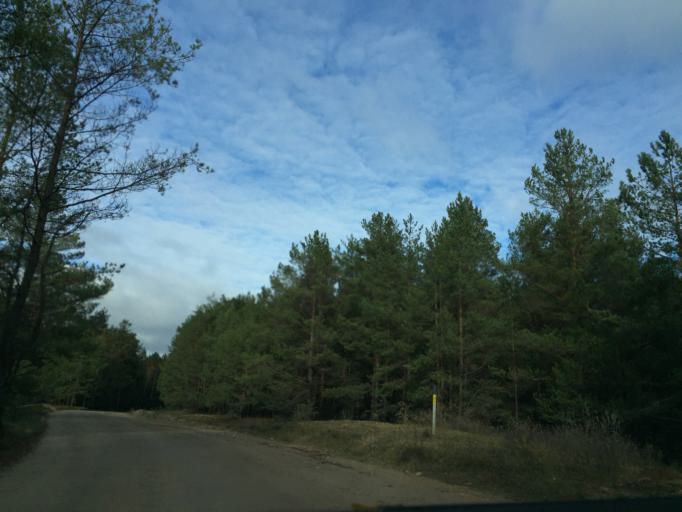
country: LV
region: Carnikava
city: Carnikava
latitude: 57.1389
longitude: 24.2661
